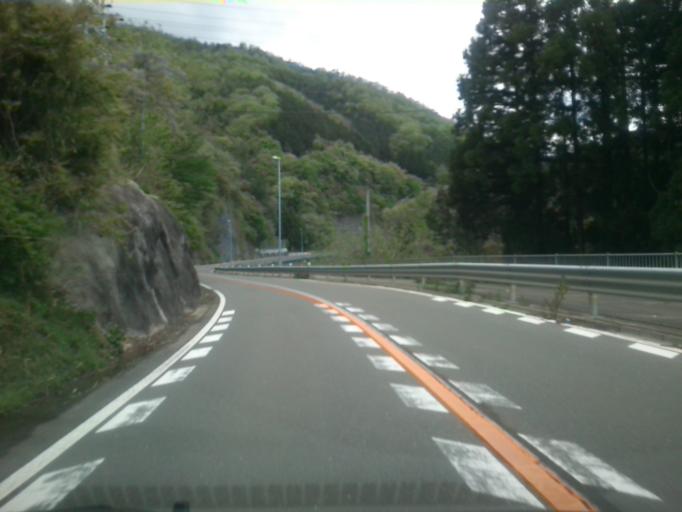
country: JP
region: Kyoto
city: Ayabe
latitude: 35.2010
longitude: 135.4224
